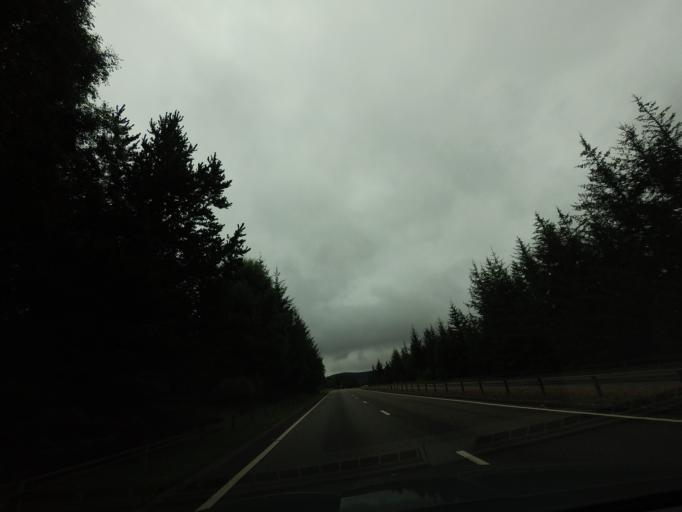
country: GB
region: Scotland
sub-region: Highland
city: Inverness
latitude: 57.3962
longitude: -4.1269
